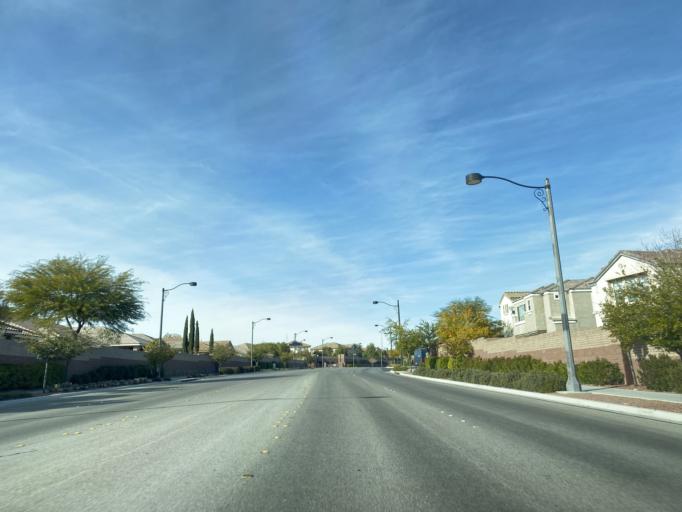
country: US
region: Nevada
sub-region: Clark County
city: Summerlin South
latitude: 36.3028
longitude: -115.3205
